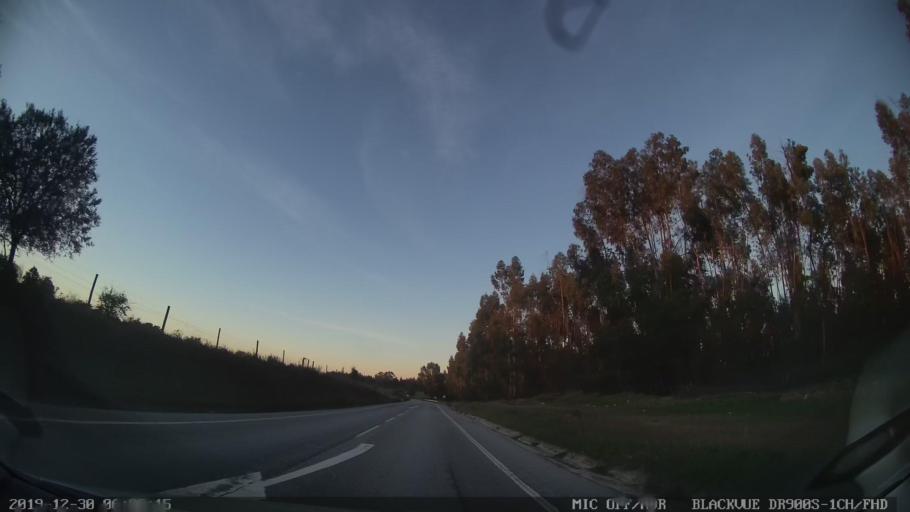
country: PT
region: Castelo Branco
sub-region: Idanha-A-Nova
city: Idanha-a-Nova
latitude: 40.0507
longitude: -7.2448
